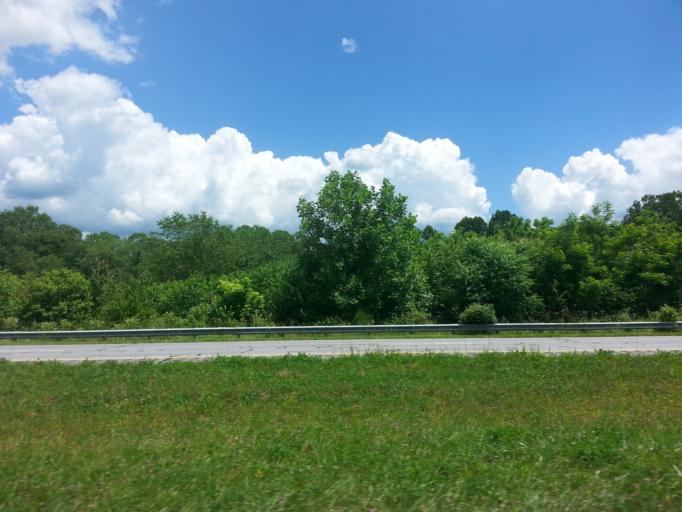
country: US
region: North Carolina
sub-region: Cherokee County
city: Andrews
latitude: 35.1960
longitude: -83.8531
